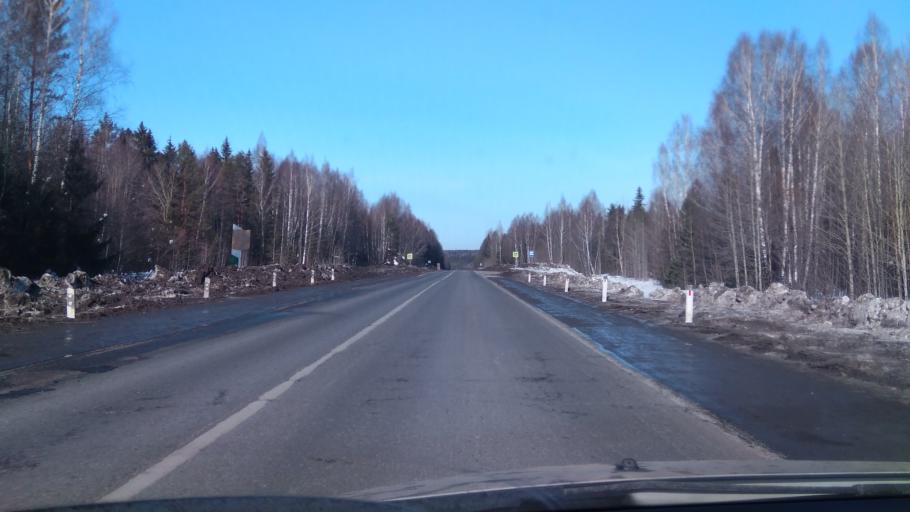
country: RU
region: Perm
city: Kukushtan
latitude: 57.5775
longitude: 56.5577
